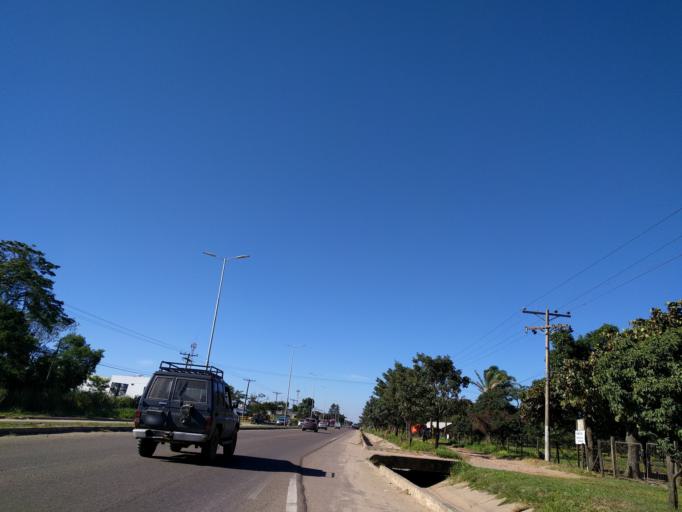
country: BO
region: Santa Cruz
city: Santa Cruz de la Sierra
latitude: -17.8660
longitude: -63.2693
